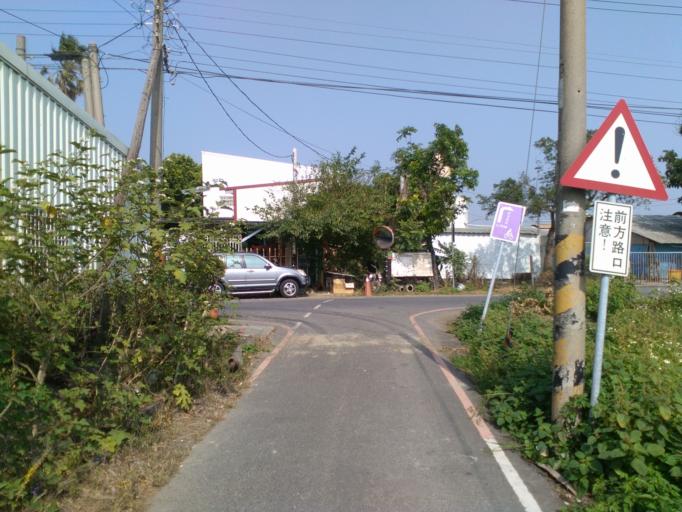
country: TW
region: Taiwan
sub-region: Chiayi
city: Taibao
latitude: 23.5645
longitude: 120.3231
